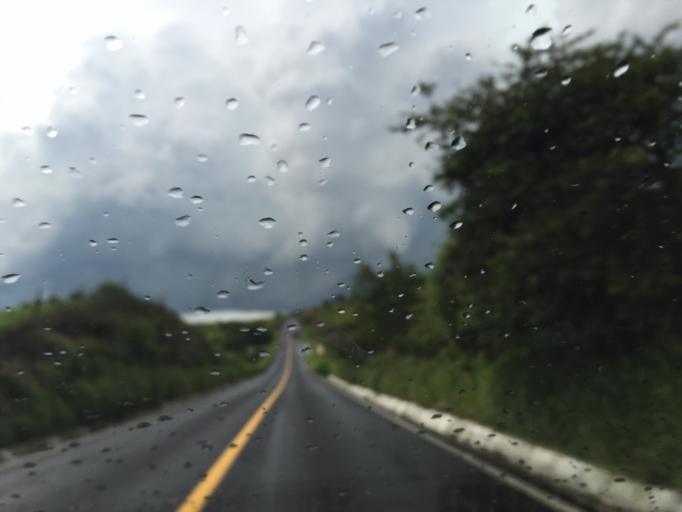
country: MX
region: Colima
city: Queseria
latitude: 19.3974
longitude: -103.5564
